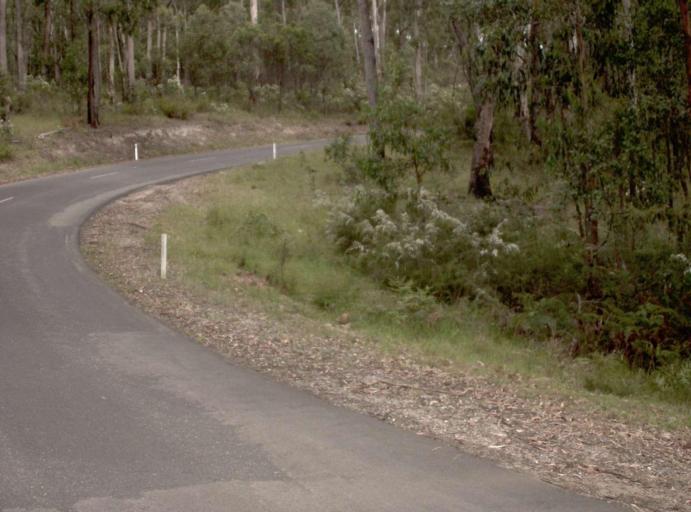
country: AU
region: Victoria
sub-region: East Gippsland
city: Bairnsdale
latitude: -37.7078
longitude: 147.5929
